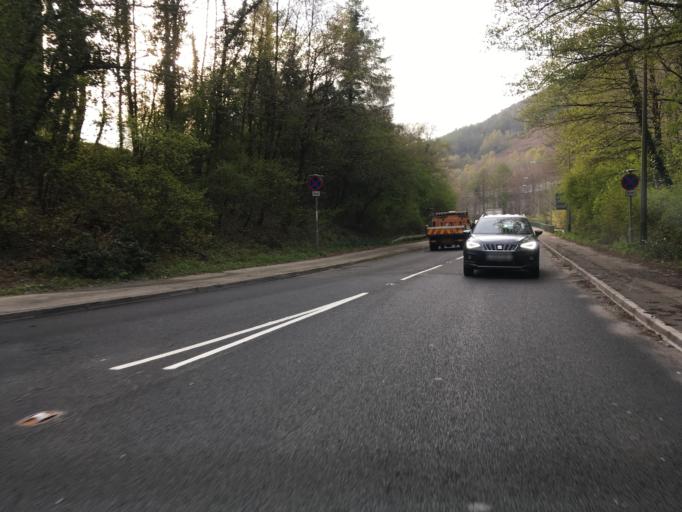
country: GB
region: Wales
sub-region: Caerphilly County Borough
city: Crosskeys
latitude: 51.6163
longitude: -3.1367
